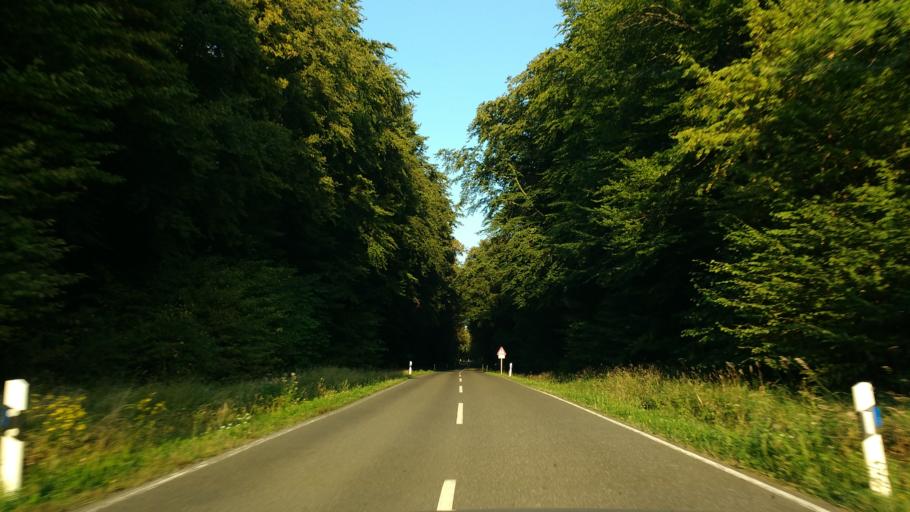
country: DE
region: Bavaria
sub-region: Regierungsbezirk Unterfranken
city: Fuchsstadt
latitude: 50.0879
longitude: 9.9405
